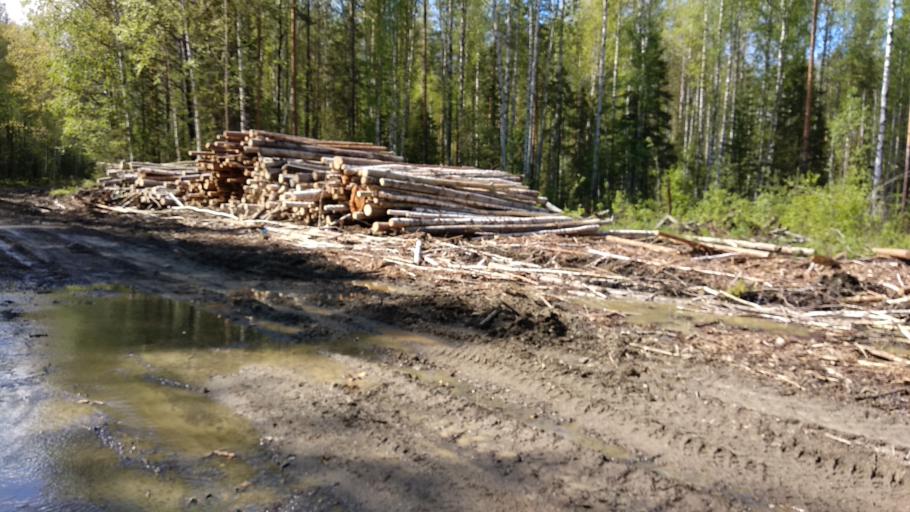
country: RU
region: Sverdlovsk
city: Karpinsk
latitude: 59.6999
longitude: 59.5593
